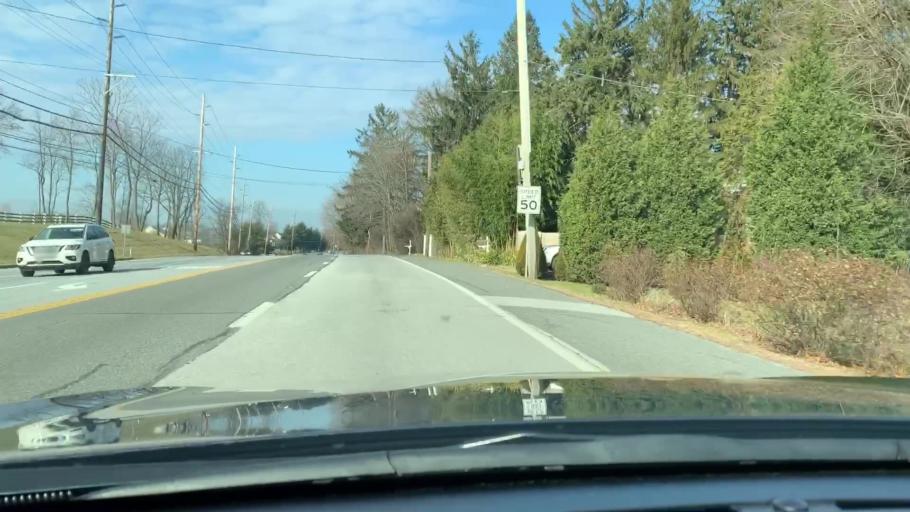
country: US
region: Pennsylvania
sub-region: Delaware County
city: Wayne
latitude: 40.0005
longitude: -75.4104
